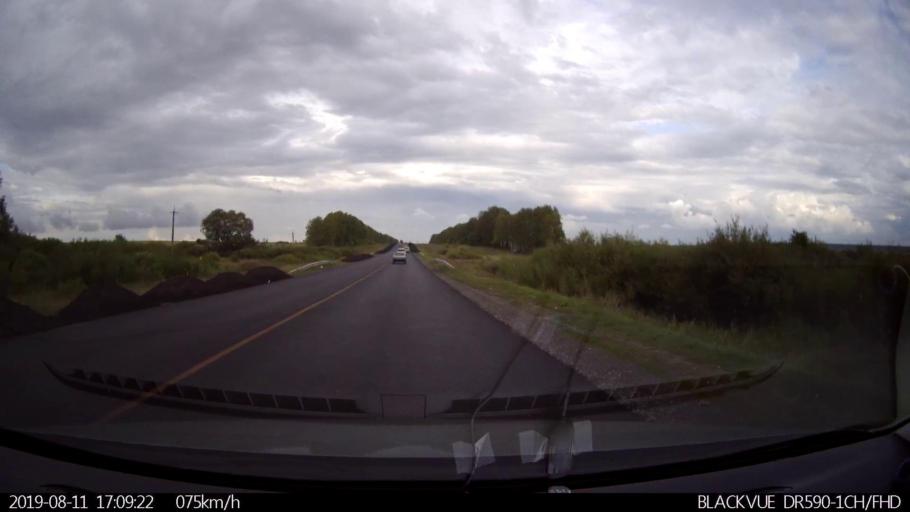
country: RU
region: Ulyanovsk
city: Mayna
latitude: 54.2964
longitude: 47.8544
